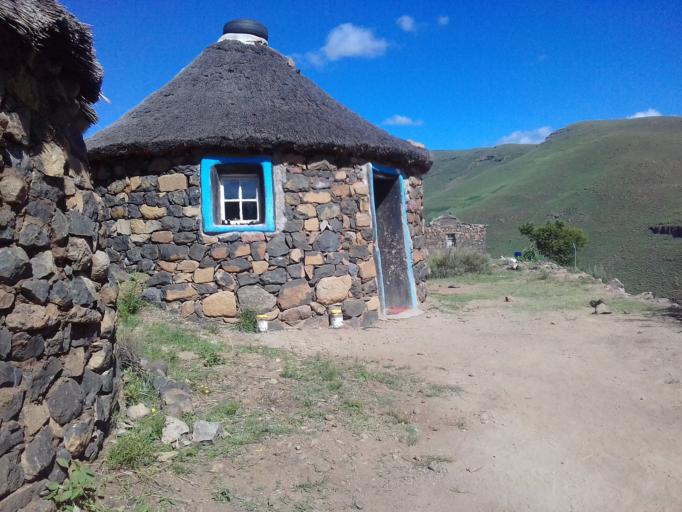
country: LS
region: Thaba-Tseka
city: Thaba-Tseka
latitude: -29.5242
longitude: 28.5800
